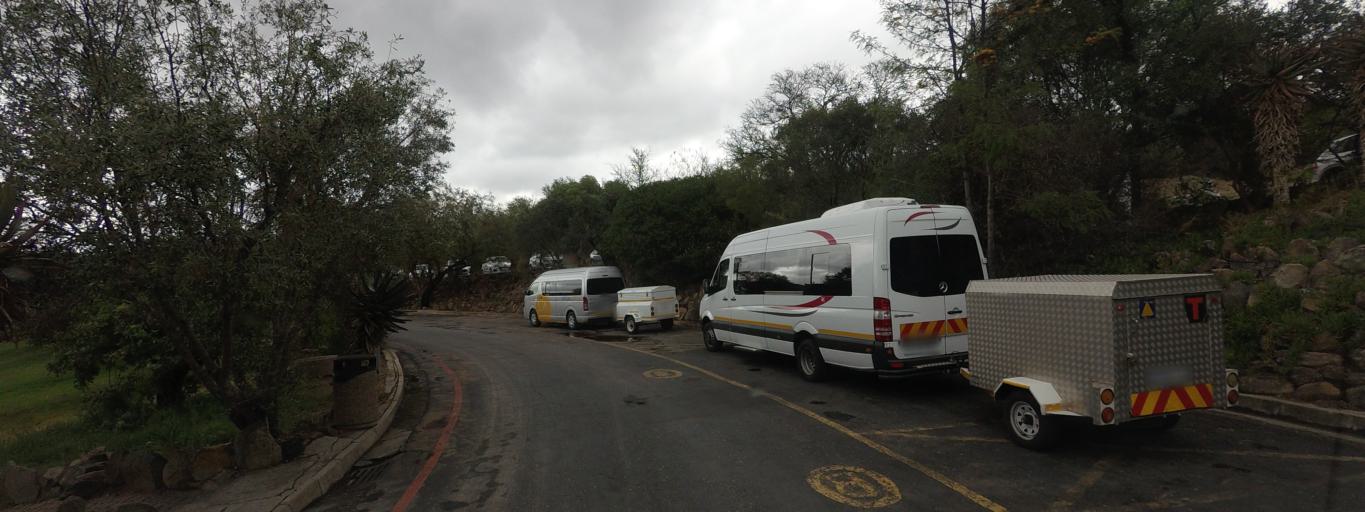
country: ZA
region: Western Cape
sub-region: Eden District Municipality
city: Oudtshoorn
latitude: -33.3934
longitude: 22.2142
